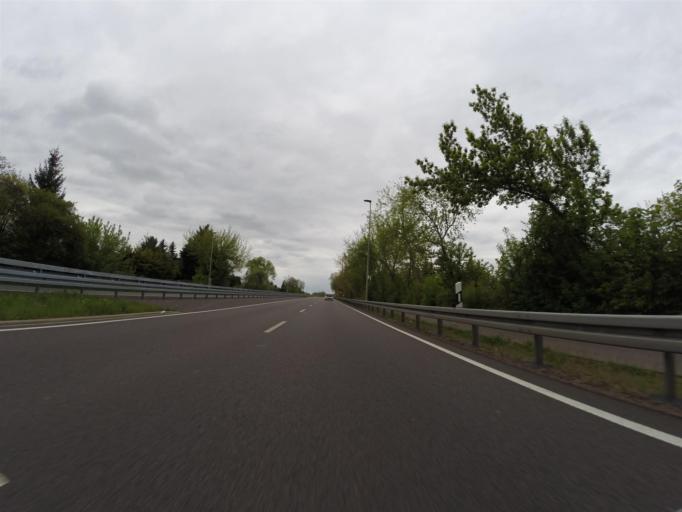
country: DE
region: Saxony-Anhalt
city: Schkopau
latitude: 51.3809
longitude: 11.9814
